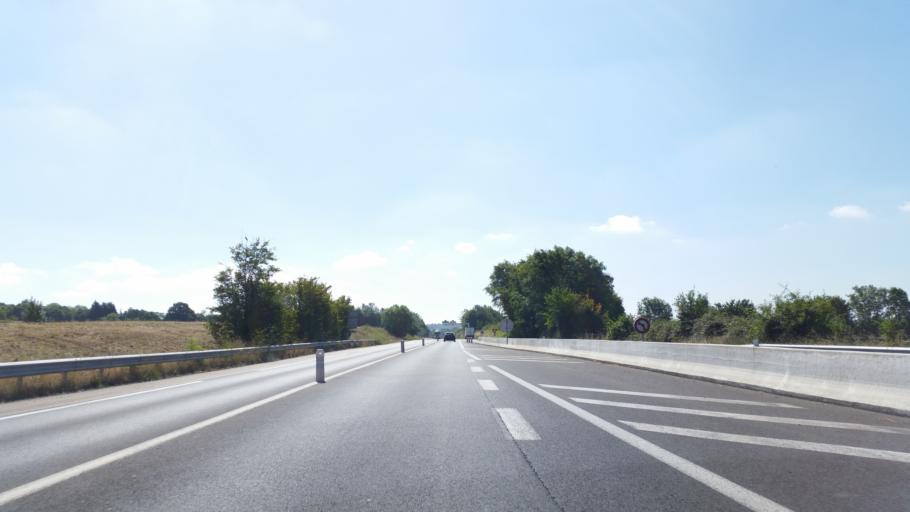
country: FR
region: Lower Normandy
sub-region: Departement du Calvados
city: Saint-Gatien-des-Bois
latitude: 49.2888
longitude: 0.2049
